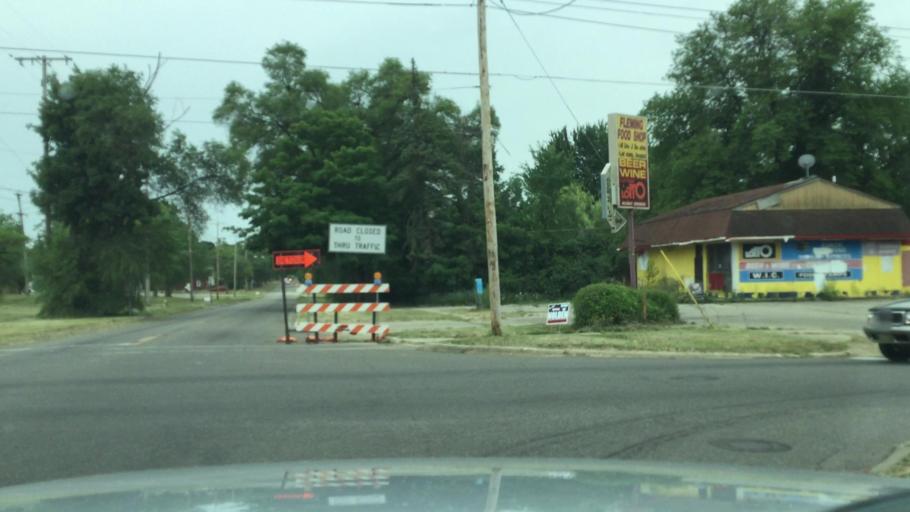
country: US
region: Michigan
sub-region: Genesee County
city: Beecher
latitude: 43.0540
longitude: -83.7236
